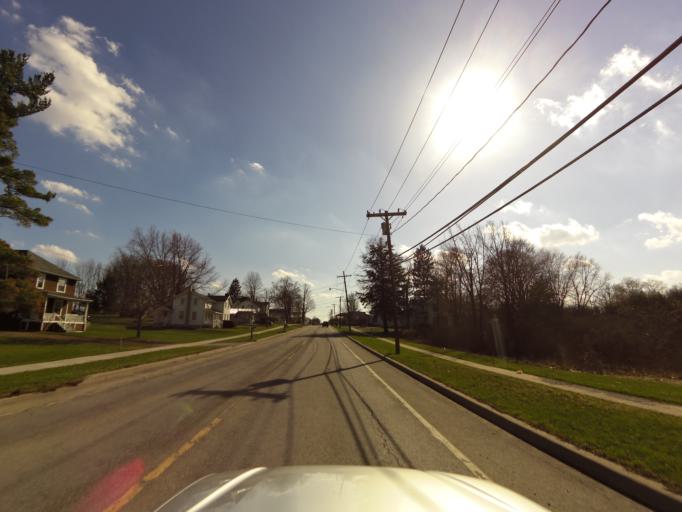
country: US
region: New York
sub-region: Wyoming County
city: Castile
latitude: 42.6276
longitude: -78.0567
